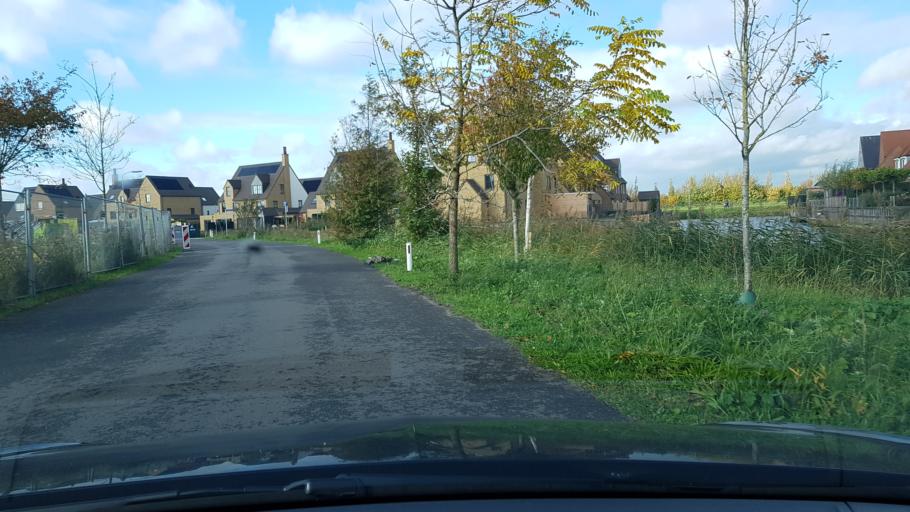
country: NL
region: North Holland
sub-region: Gemeente Haarlemmermeer
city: Hoofddorp
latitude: 52.2932
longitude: 4.6579
